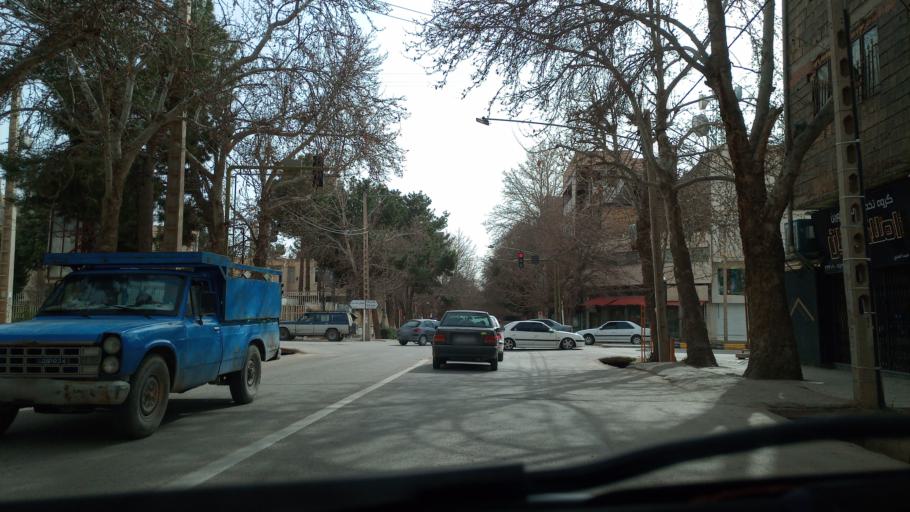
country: IR
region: Khorasan-e Shomali
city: Esfarayen
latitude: 37.0798
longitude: 57.5133
